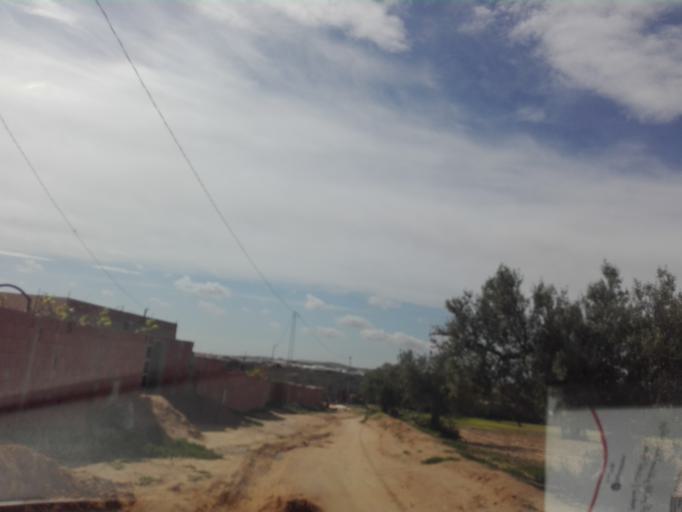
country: TN
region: Safaqis
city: Sfax
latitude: 34.7413
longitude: 10.5054
